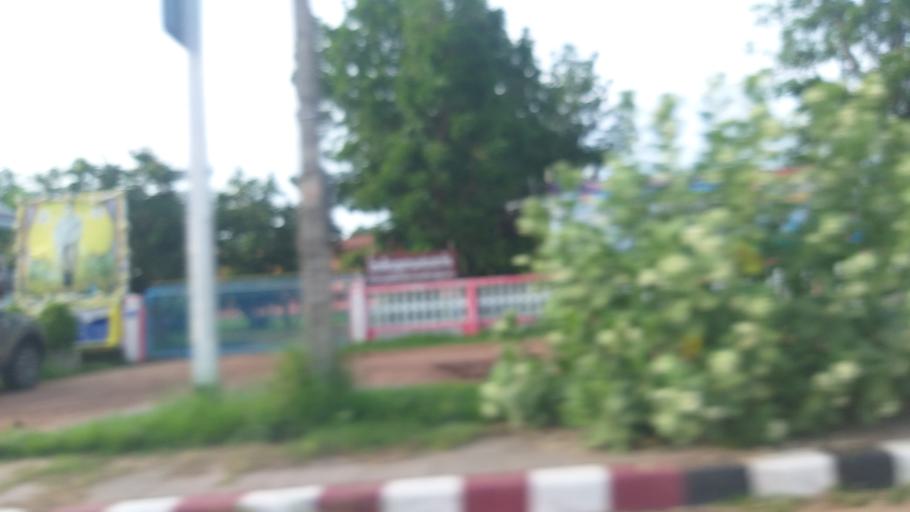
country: TH
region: Chaiyaphum
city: Ban Thaen
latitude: 16.4078
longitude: 102.3489
